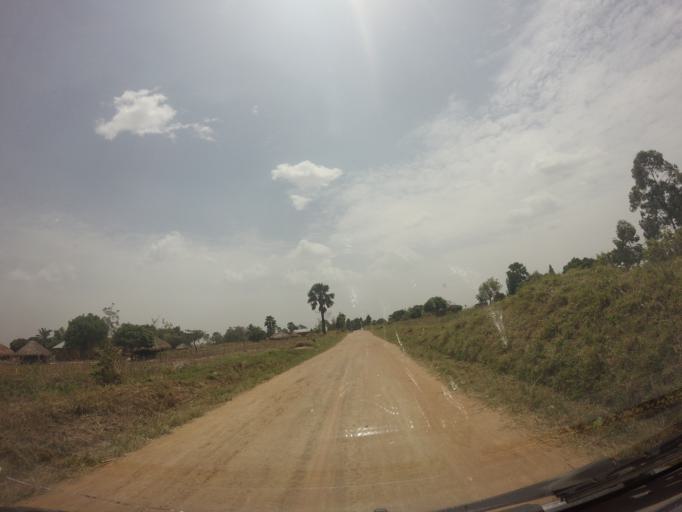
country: UG
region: Northern Region
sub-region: Arua District
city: Arua
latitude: 2.9499
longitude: 30.9137
